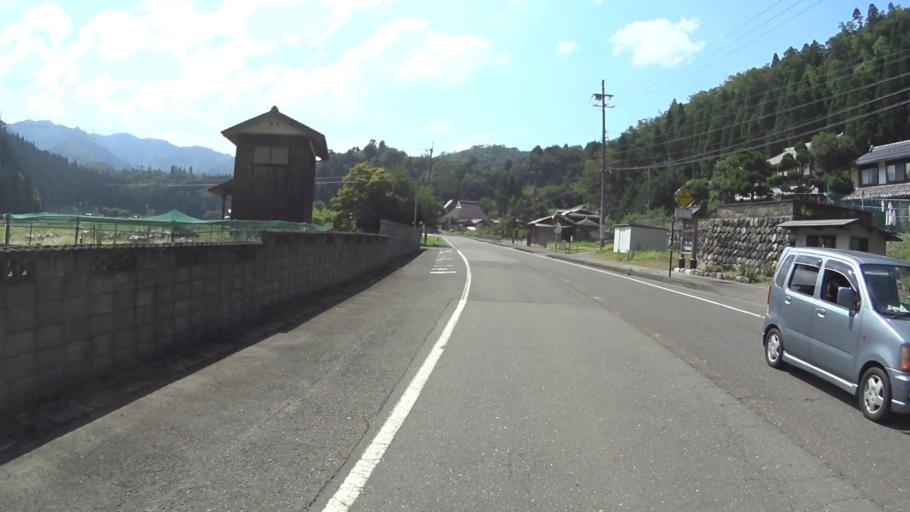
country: JP
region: Fukui
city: Obama
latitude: 35.3956
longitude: 135.5944
